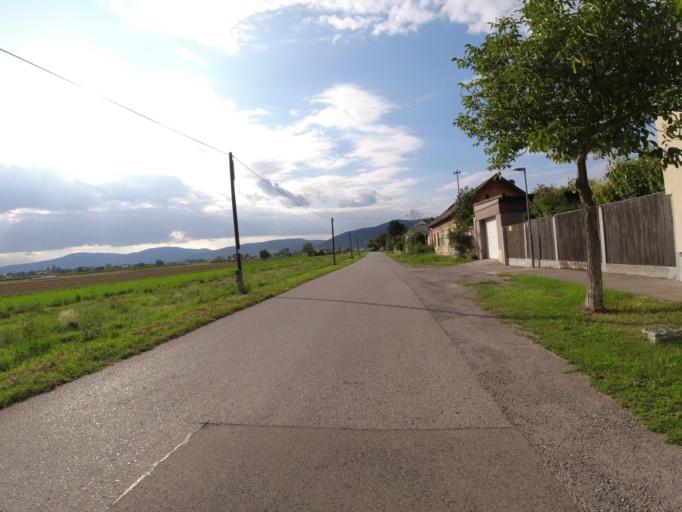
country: AT
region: Lower Austria
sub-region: Politischer Bezirk Baden
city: Traiskirchen
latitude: 48.0111
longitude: 16.2833
